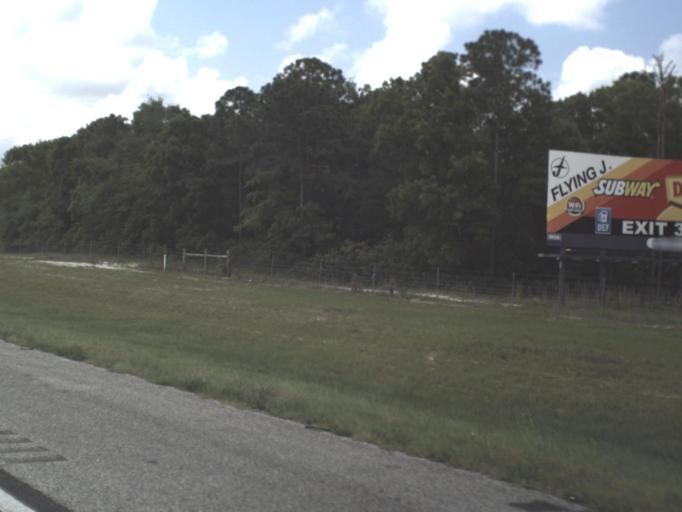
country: US
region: Florida
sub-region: Flagler County
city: Palm Coast
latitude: 29.6581
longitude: -81.2806
